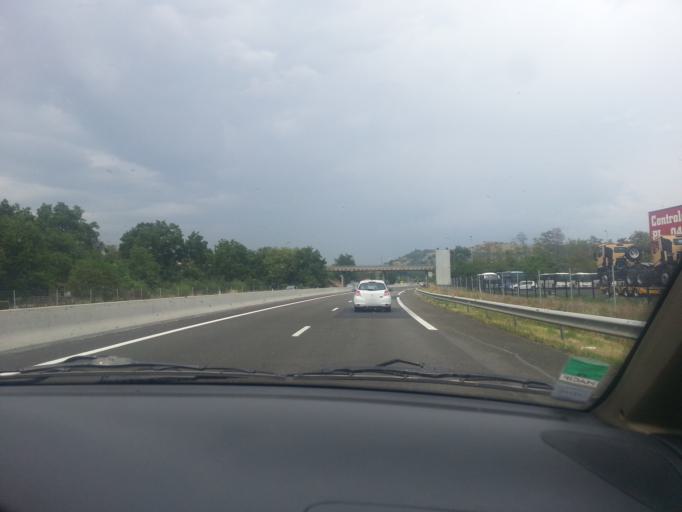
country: FR
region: Auvergne
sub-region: Departement du Puy-de-Dome
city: Issoire
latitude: 45.5367
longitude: 3.2605
